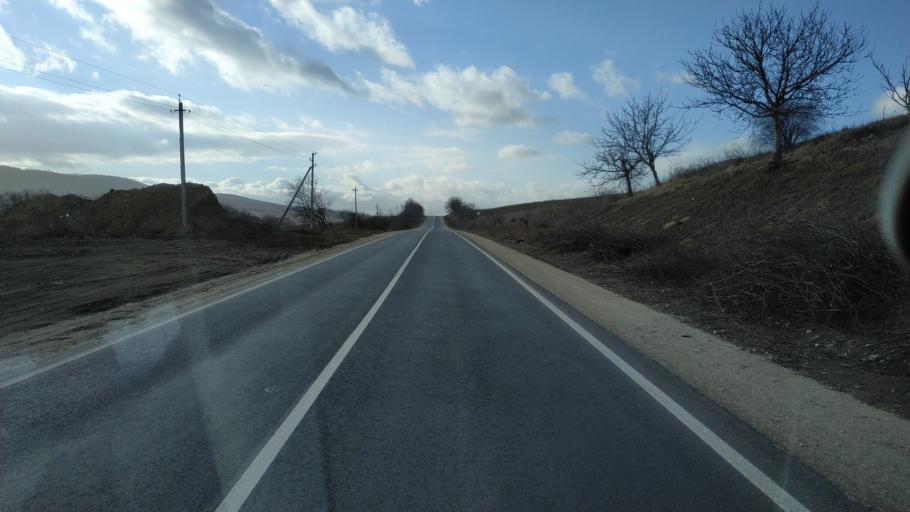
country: MD
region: Calarasi
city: Calarasi
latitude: 47.2947
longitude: 28.1678
